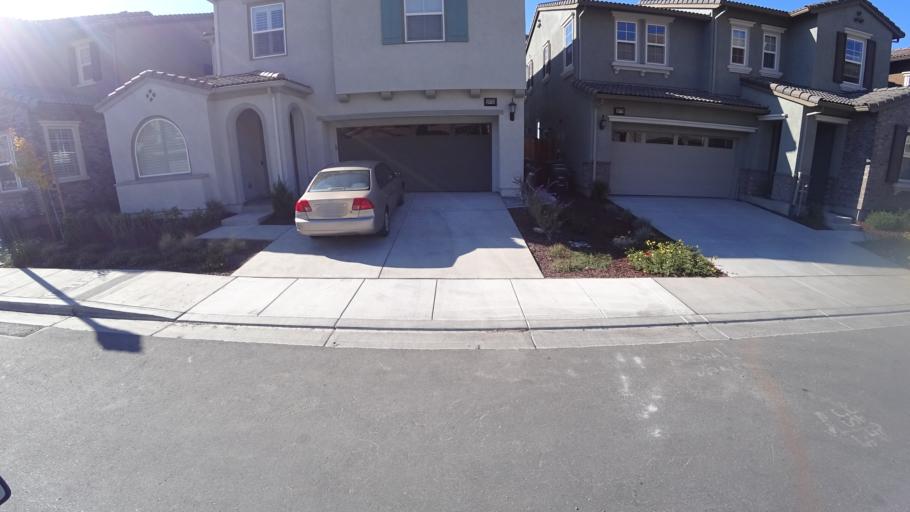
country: US
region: California
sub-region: Alameda County
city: Fairview
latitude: 37.6393
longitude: -122.0465
